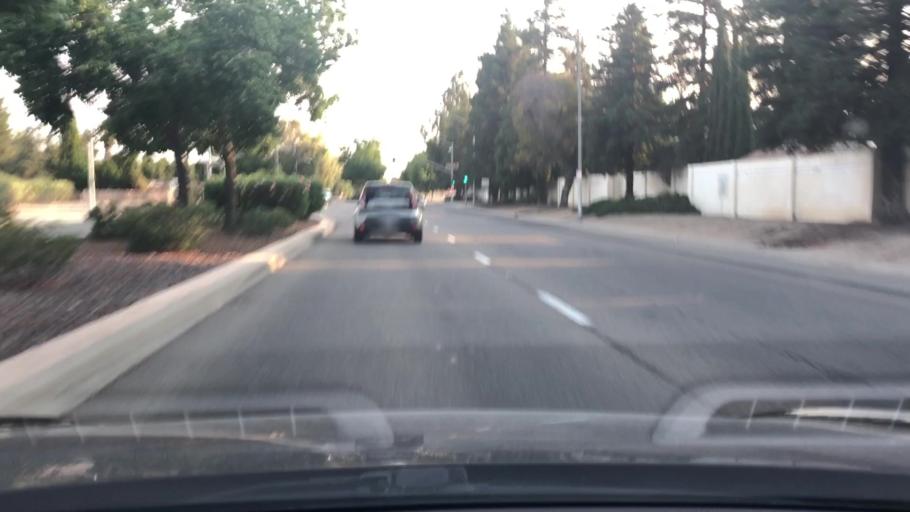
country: US
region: California
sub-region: Fresno County
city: Clovis
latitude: 36.8253
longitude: -119.7294
